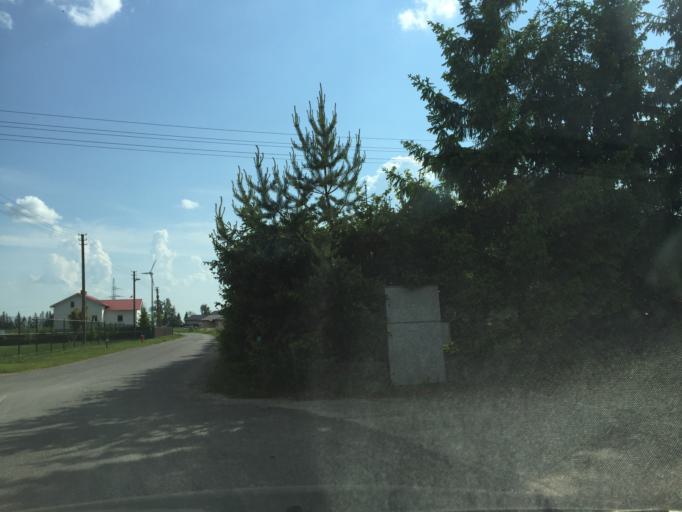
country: LT
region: Klaipedos apskritis
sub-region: Klaipeda
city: Palanga
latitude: 55.9075
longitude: 21.1245
